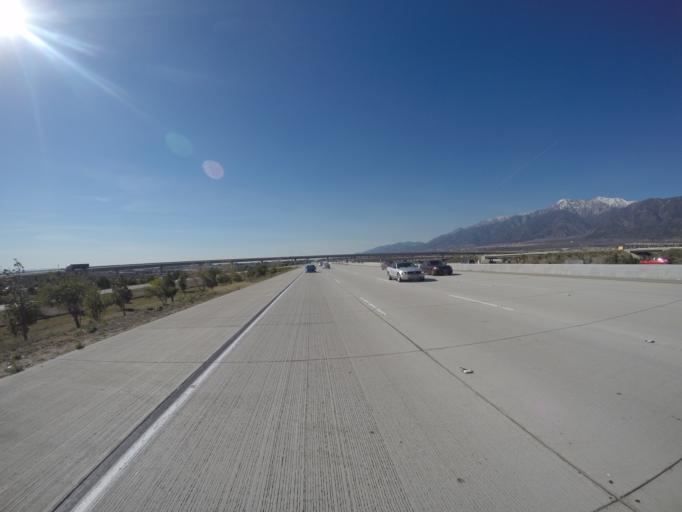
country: US
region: California
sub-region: San Bernardino County
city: Fontana
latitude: 34.1362
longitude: -117.4908
